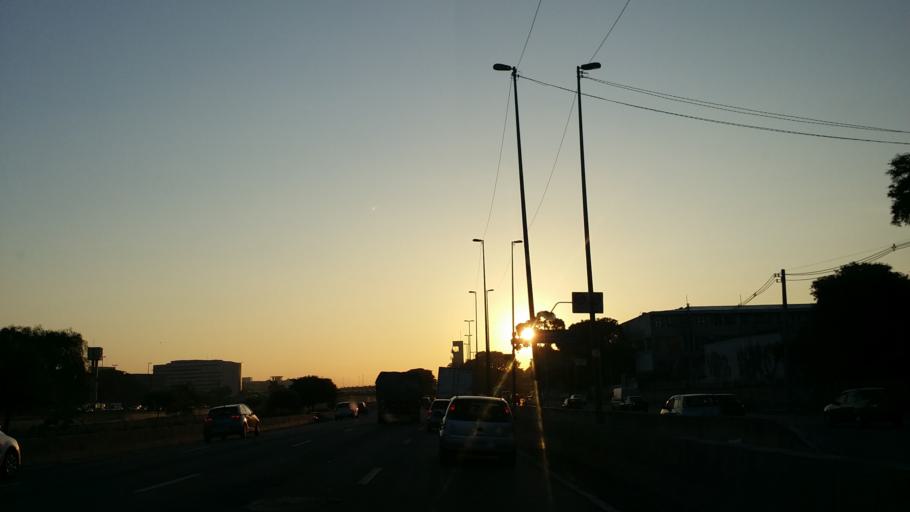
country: BR
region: Sao Paulo
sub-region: Sao Paulo
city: Sao Paulo
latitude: -23.5192
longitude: -46.6347
